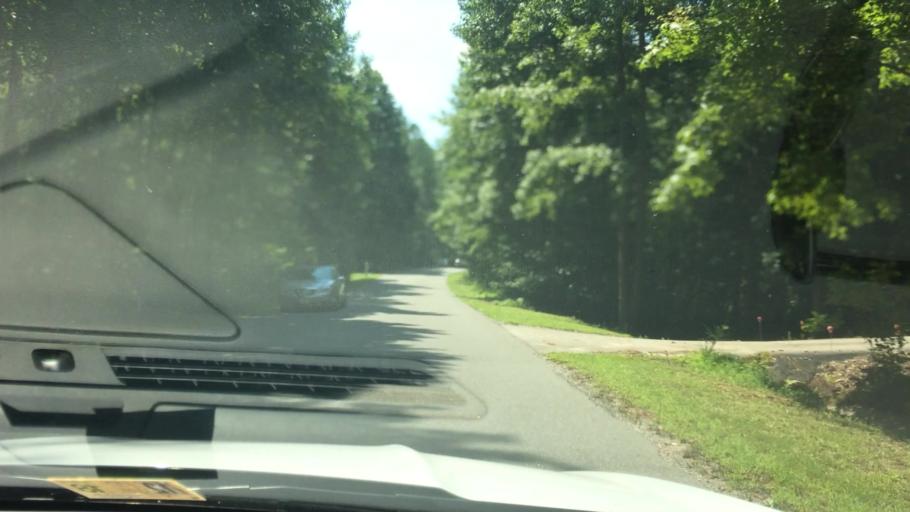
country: US
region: Virginia
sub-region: Henrico County
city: Sandston
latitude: 37.5017
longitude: -77.1701
